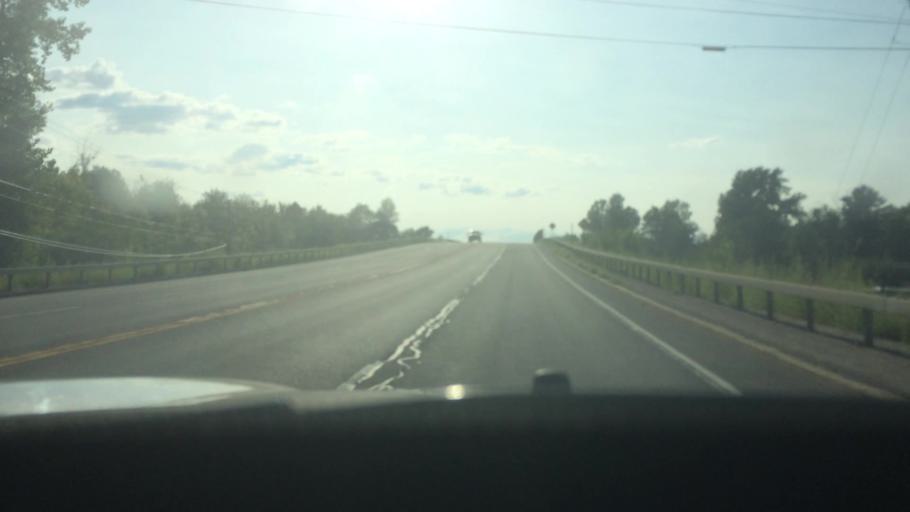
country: US
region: New York
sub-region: St. Lawrence County
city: Potsdam
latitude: 44.6673
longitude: -75.0060
